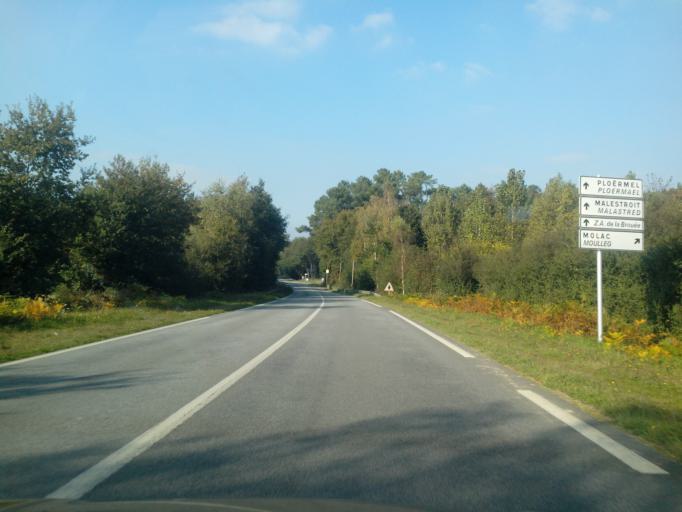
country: FR
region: Brittany
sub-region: Departement du Morbihan
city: Molac
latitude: 47.7198
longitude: -2.4390
